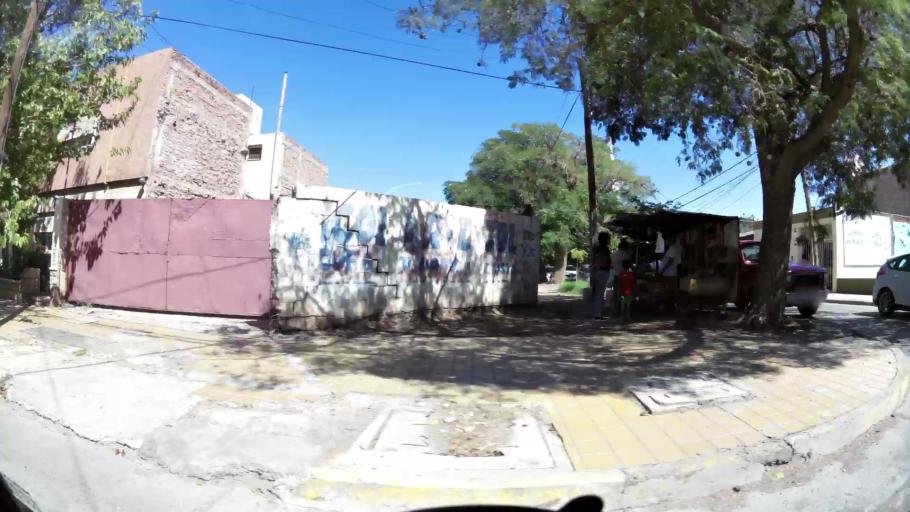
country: AR
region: San Juan
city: San Juan
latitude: -31.5462
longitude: -68.5235
